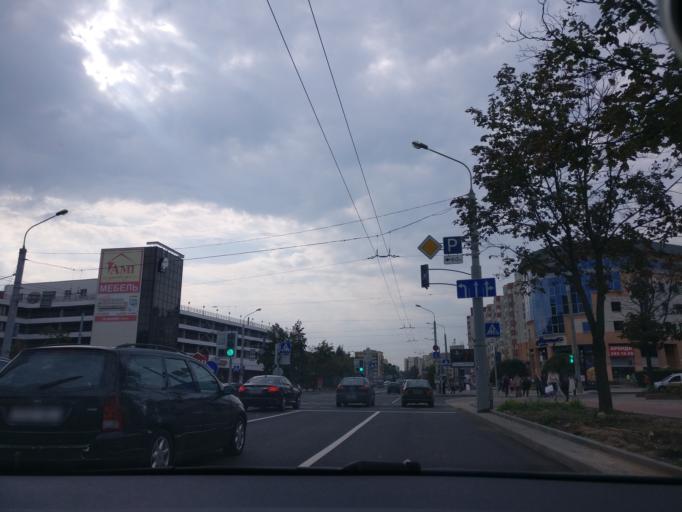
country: BY
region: Minsk
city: Minsk
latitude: 53.9225
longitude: 27.5787
